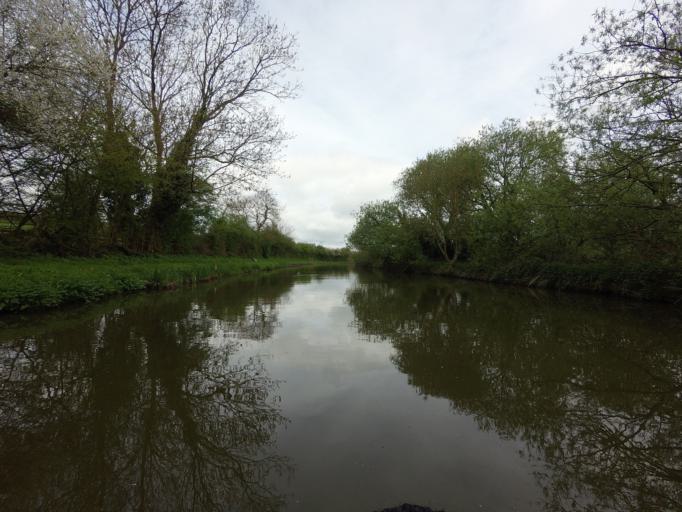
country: GB
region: England
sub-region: Milton Keynes
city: Water Eaton
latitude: 51.9497
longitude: -0.7076
